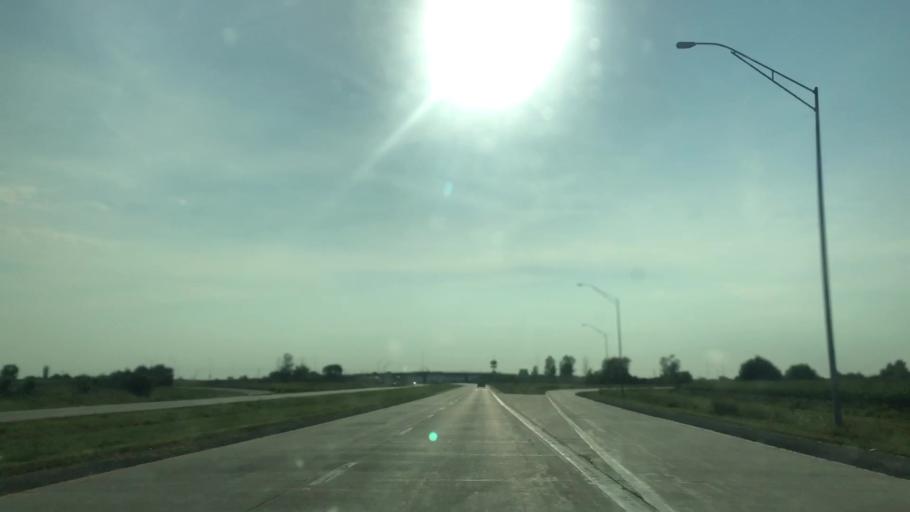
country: US
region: Iowa
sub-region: Story County
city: Nevada
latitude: 42.0081
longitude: -93.4276
